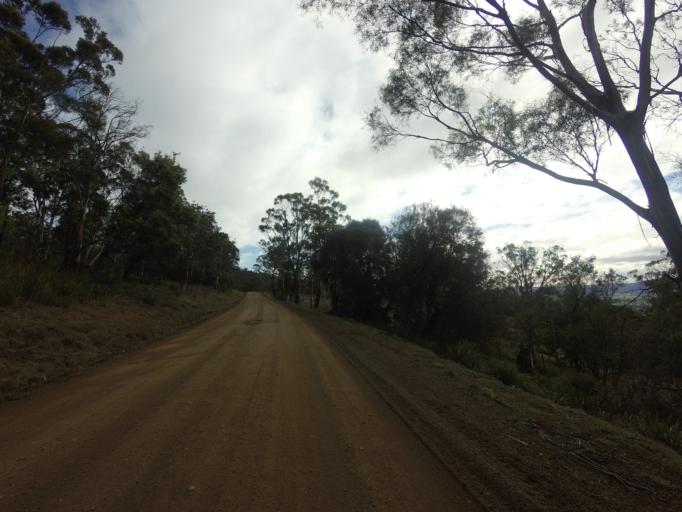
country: AU
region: Tasmania
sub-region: Derwent Valley
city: New Norfolk
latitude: -42.7377
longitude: 146.8701
